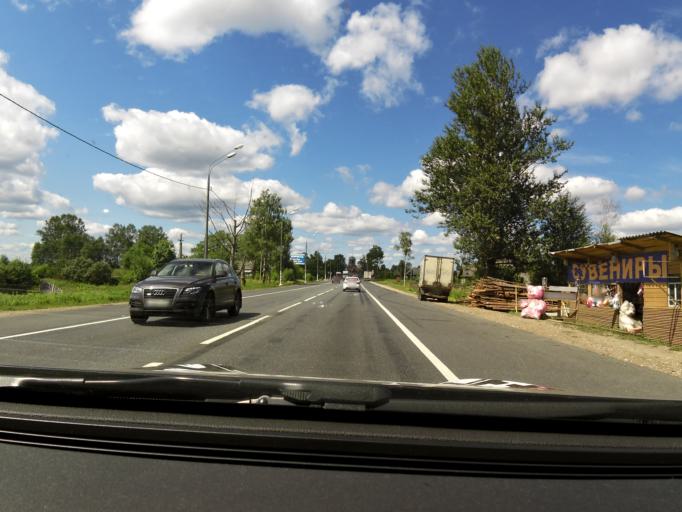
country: RU
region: Tverskaya
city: Kuzhenkino
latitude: 57.7218
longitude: 34.0956
